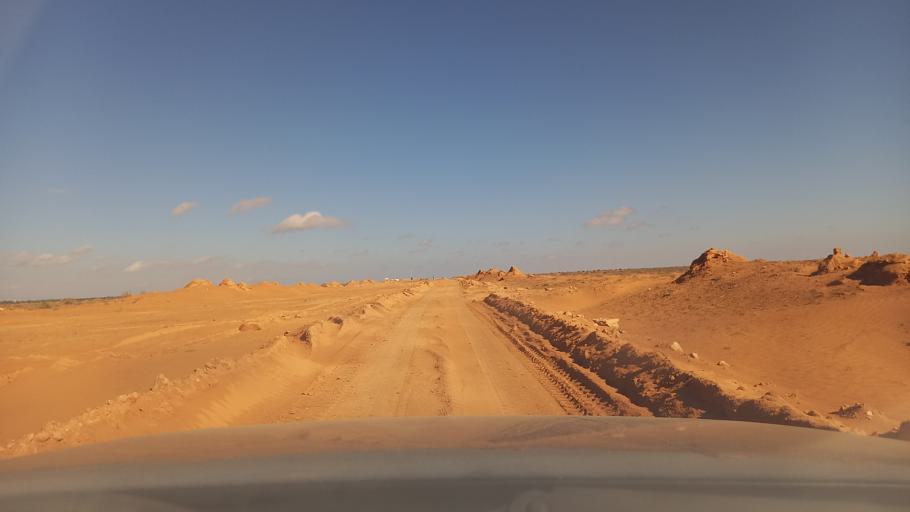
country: TN
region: Madanin
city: Medenine
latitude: 33.2445
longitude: 10.5595
